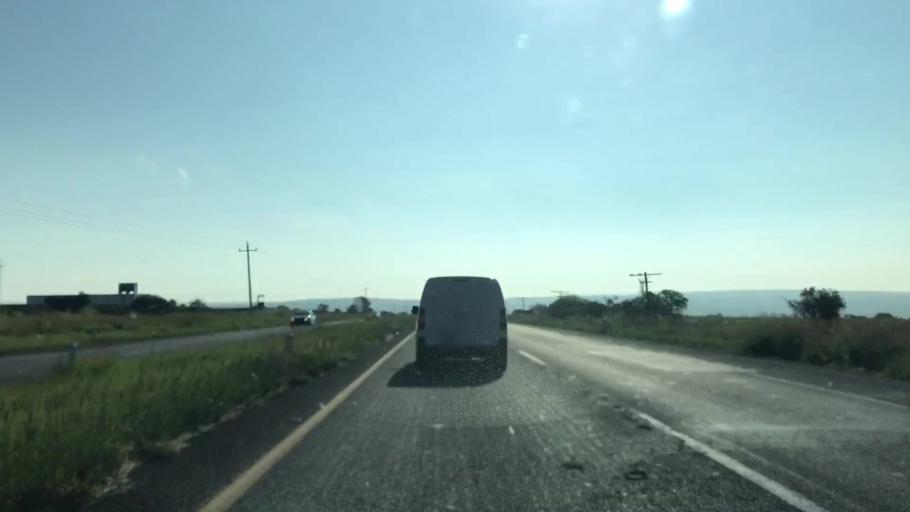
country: MX
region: Jalisco
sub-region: San Juan de los Lagos
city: Mezquitic de la Magdalena
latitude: 21.2895
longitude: -102.2024
